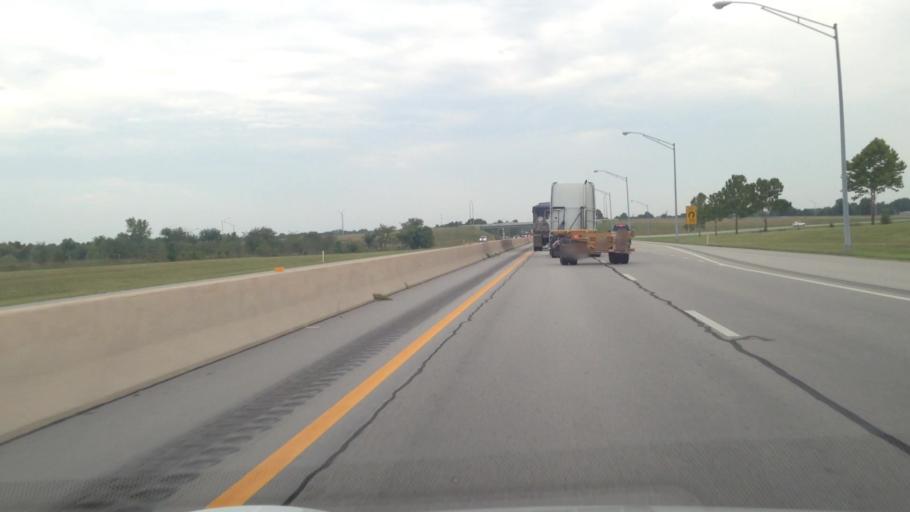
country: US
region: Oklahoma
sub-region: Ottawa County
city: Miami
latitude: 36.8693
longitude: -94.8482
